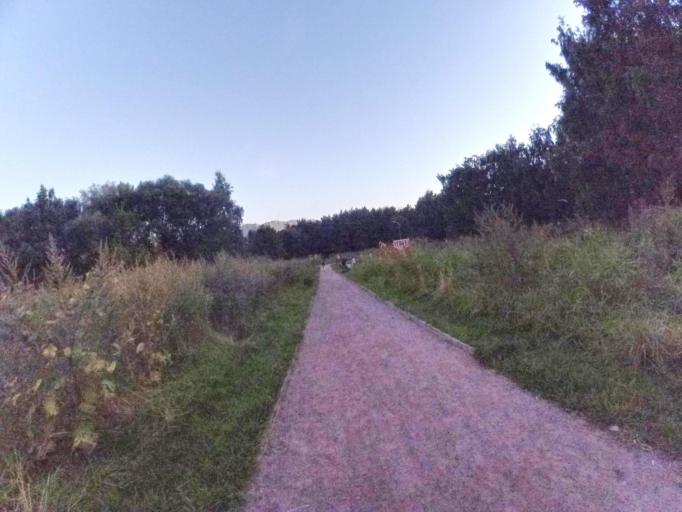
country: RU
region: Moscow
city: Strogino
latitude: 55.8217
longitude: 37.3963
